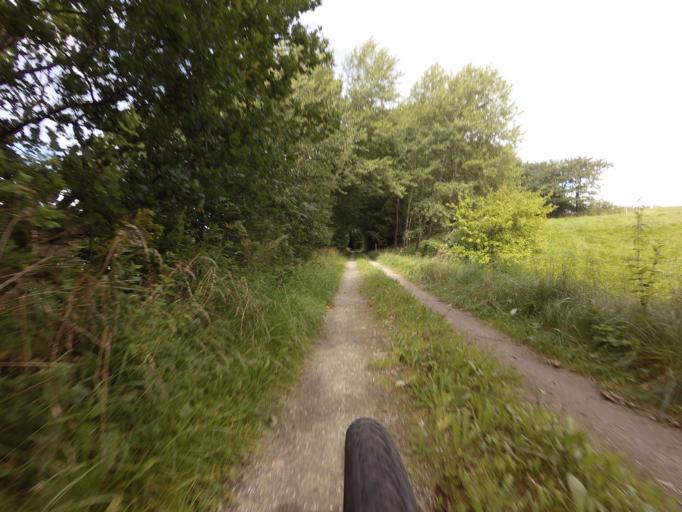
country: DK
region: Central Jutland
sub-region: Syddjurs Kommune
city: Ryomgard
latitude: 56.3975
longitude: 10.5319
